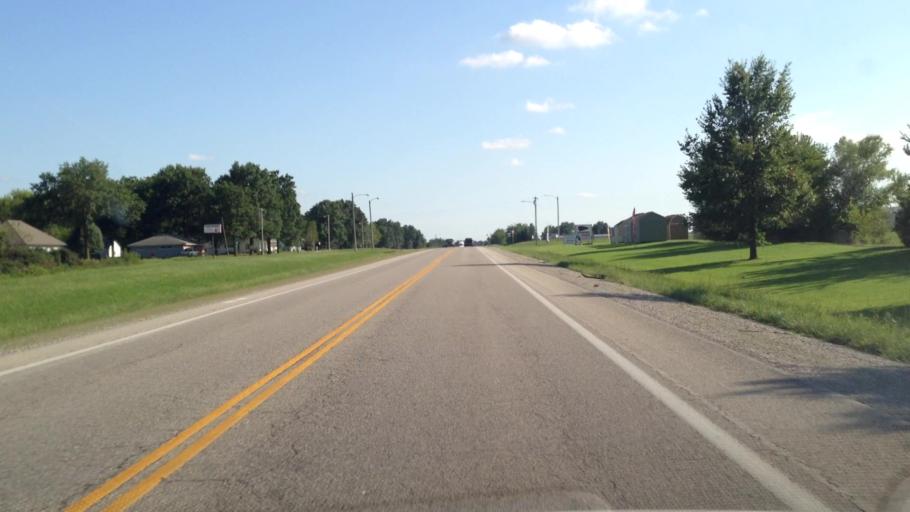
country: US
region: Kansas
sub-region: Crawford County
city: Arma
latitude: 37.5484
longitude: -94.7101
